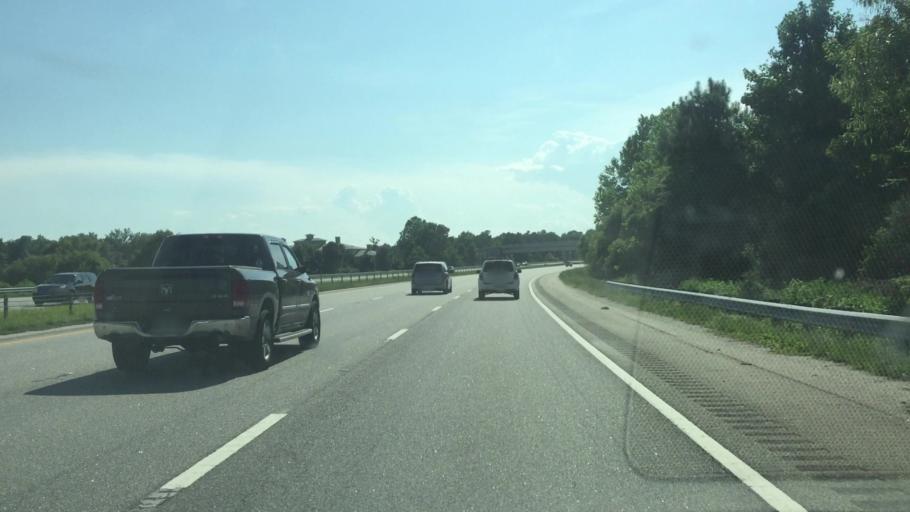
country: US
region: South Carolina
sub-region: Horry County
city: North Myrtle Beach
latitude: 33.8149
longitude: -78.7452
